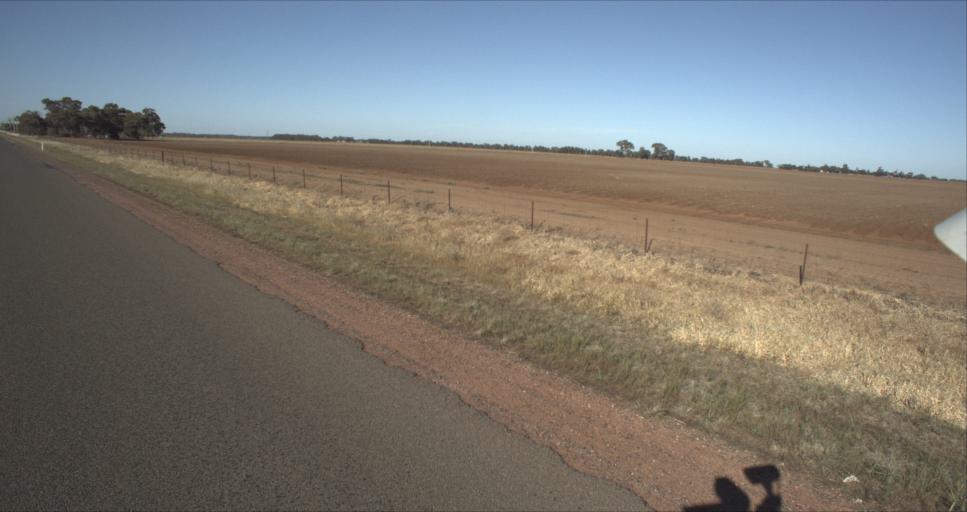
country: AU
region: New South Wales
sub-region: Leeton
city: Leeton
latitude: -34.5738
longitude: 146.2630
